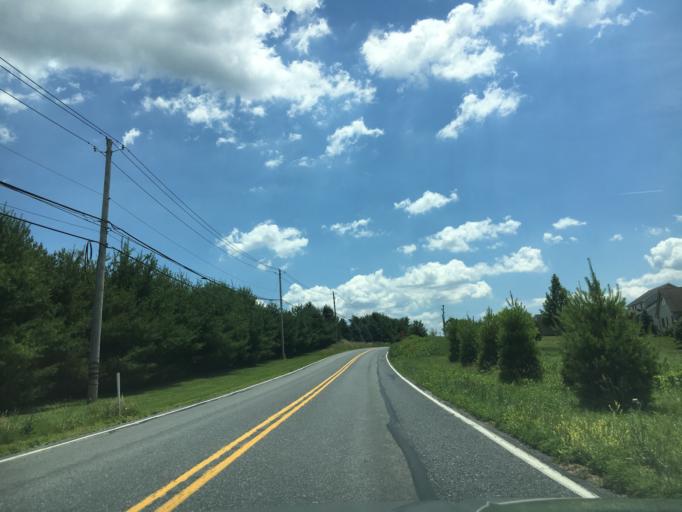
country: US
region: Pennsylvania
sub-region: Lehigh County
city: Schnecksville
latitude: 40.6903
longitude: -75.5888
